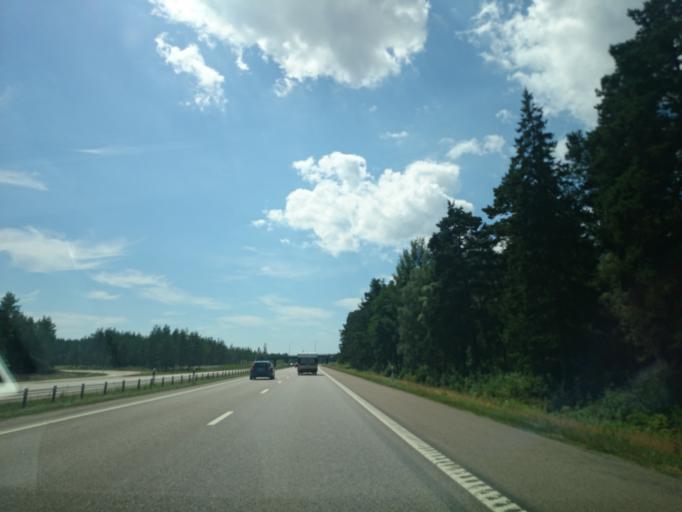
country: SE
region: Kalmar
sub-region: Kalmar Kommun
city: Lindsdal
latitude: 56.7166
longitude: 16.3156
